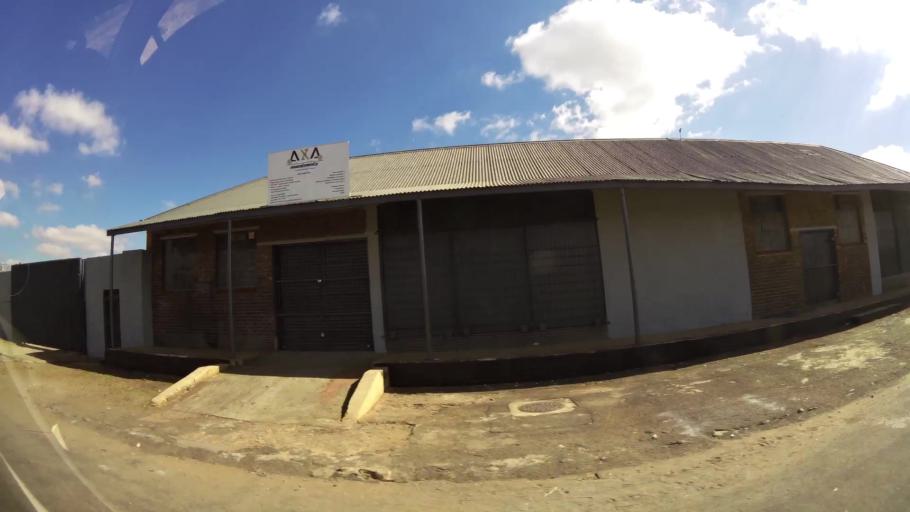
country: ZA
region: Gauteng
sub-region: West Rand District Municipality
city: Krugersdorp
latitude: -26.1241
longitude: 27.8068
